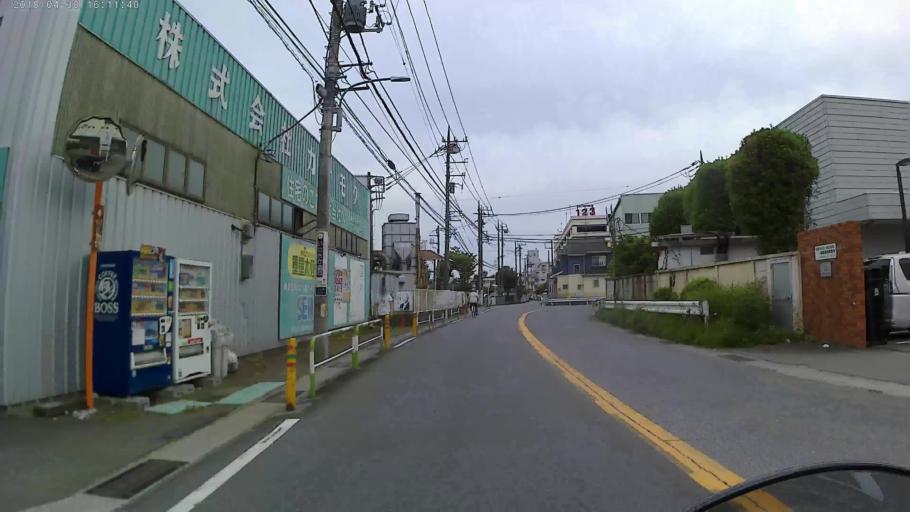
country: JP
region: Kanagawa
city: Minami-rinkan
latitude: 35.5004
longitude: 139.4284
